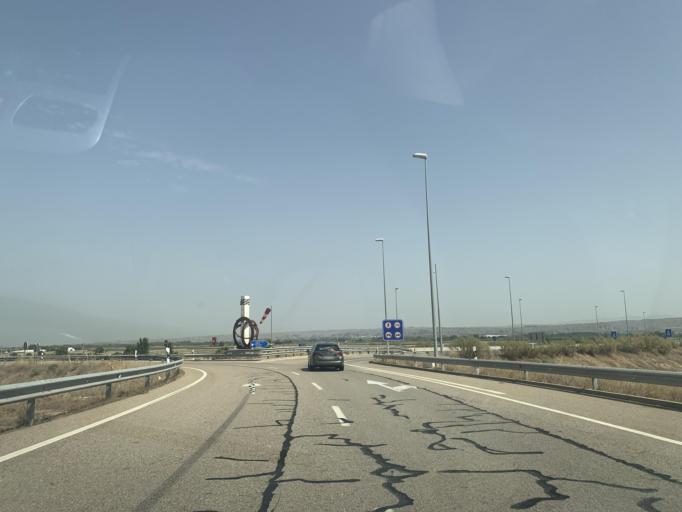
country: ES
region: Aragon
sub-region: Provincia de Zaragoza
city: Nuez de Ebro
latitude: 41.5455
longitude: -0.6946
